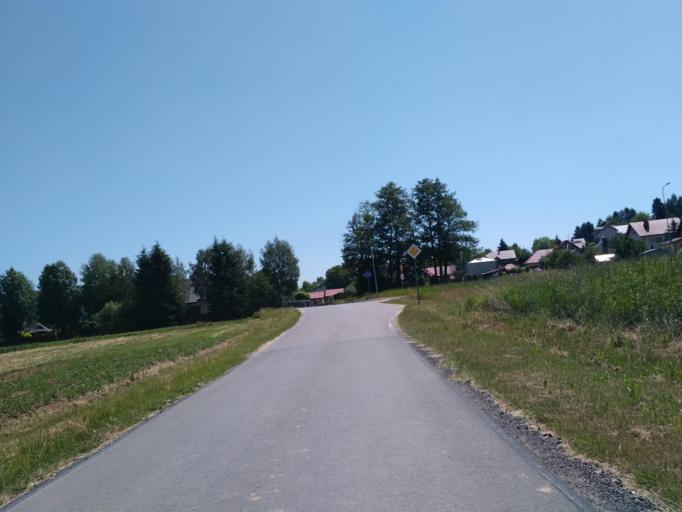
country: PL
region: Subcarpathian Voivodeship
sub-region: Powiat krosnienski
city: Korczyna
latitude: 49.7129
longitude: 21.7834
